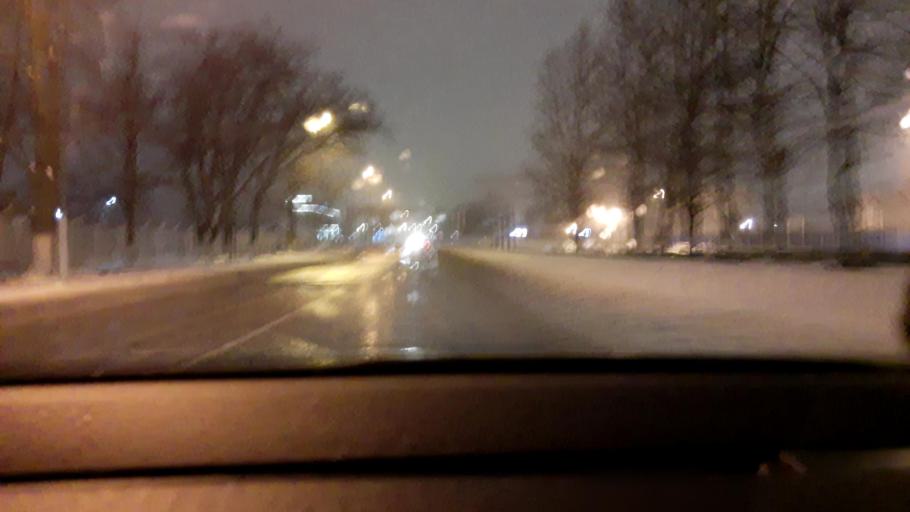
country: RU
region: Moskovskaya
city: Yakovlevskoye
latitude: 55.4282
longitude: 37.8770
